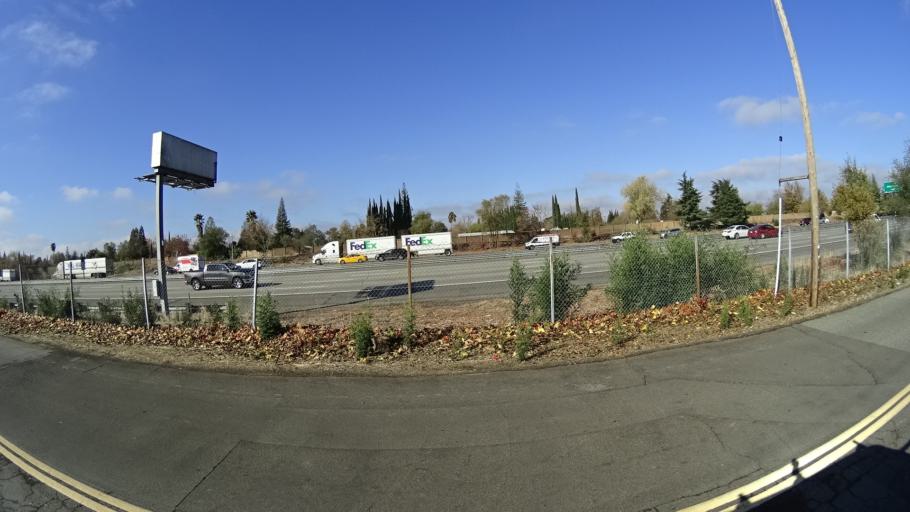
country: US
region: California
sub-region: Sacramento County
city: Antelope
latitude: 38.6932
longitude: -121.3243
